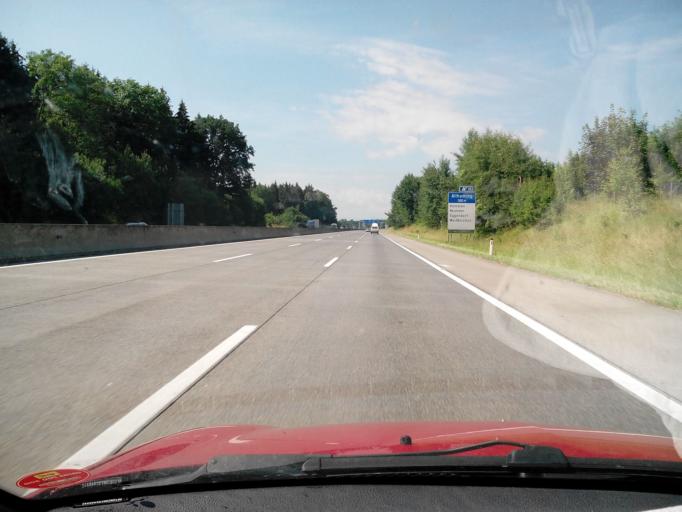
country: AT
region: Upper Austria
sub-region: Wels-Land
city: Marchtrenk
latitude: 48.1643
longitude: 14.1659
